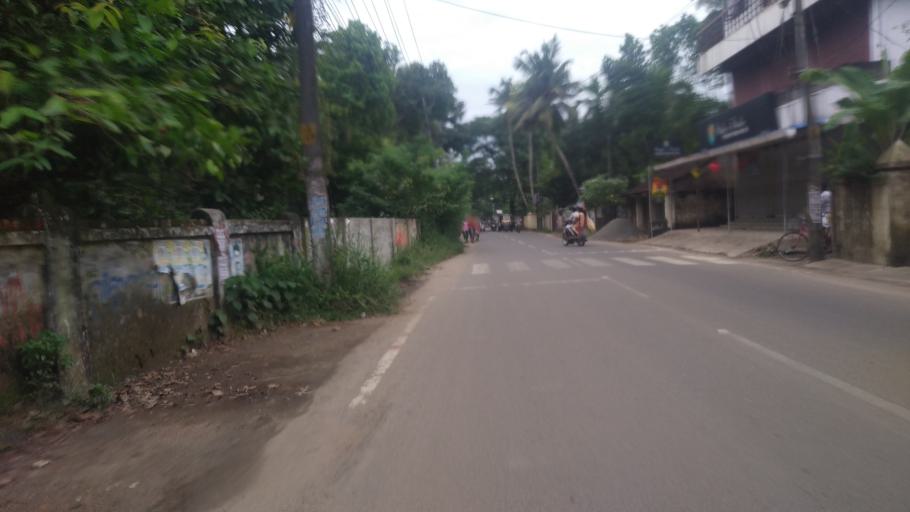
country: IN
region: Kerala
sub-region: Alappuzha
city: Arukutti
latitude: 9.8684
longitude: 76.2911
